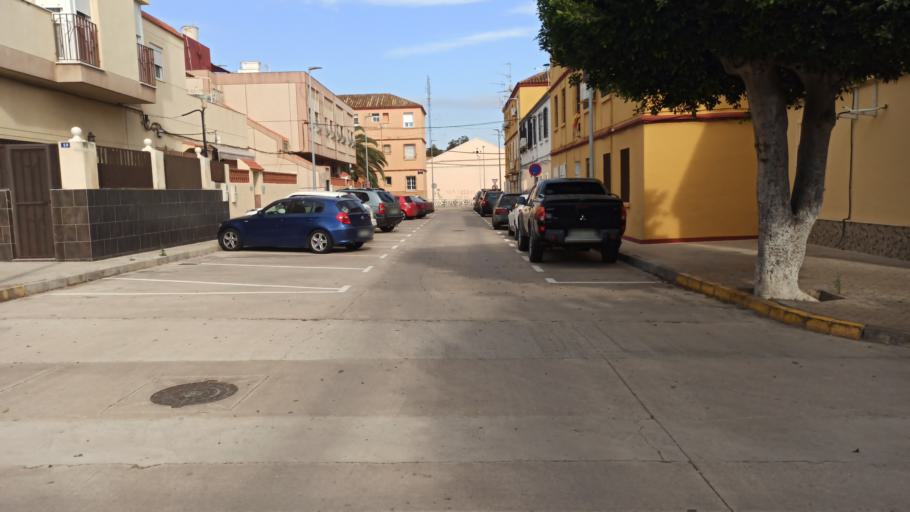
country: ES
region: Melilla
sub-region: Melilla
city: Melilla
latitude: 35.2876
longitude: -2.9502
